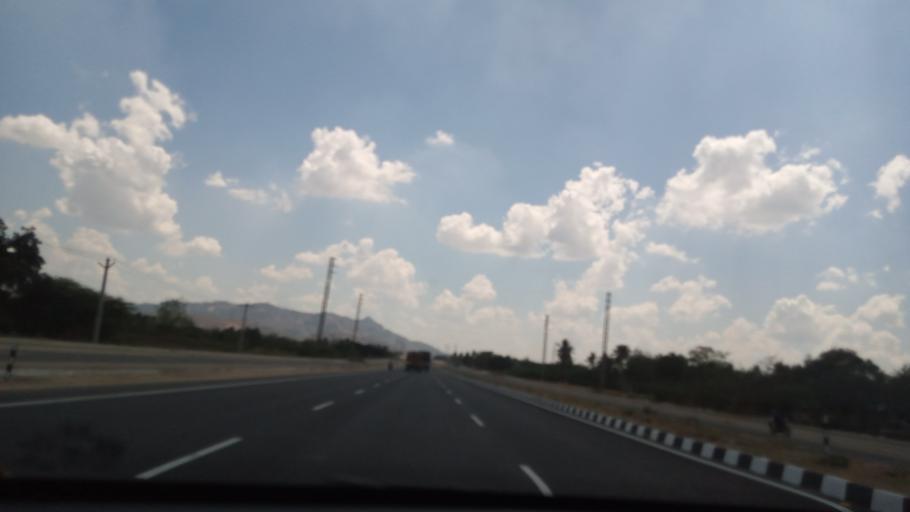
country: IN
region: Andhra Pradesh
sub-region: Chittoor
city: Pakala
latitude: 13.3689
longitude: 79.0904
